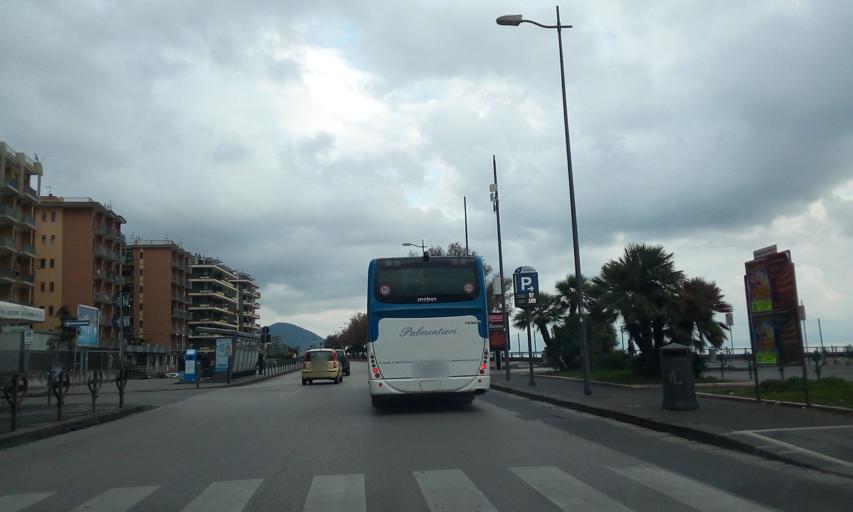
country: IT
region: Campania
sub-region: Provincia di Salerno
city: Salerno
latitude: 40.6738
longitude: 14.7706
